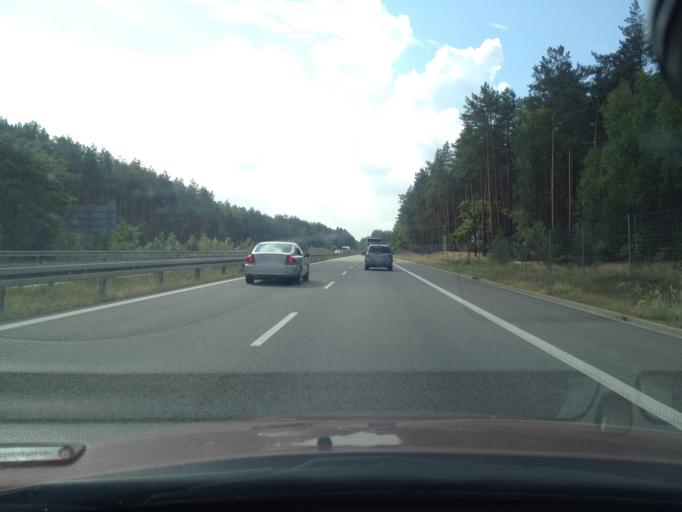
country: PL
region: West Pomeranian Voivodeship
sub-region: Powiat goleniowski
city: Goleniow
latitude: 53.6006
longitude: 14.8242
